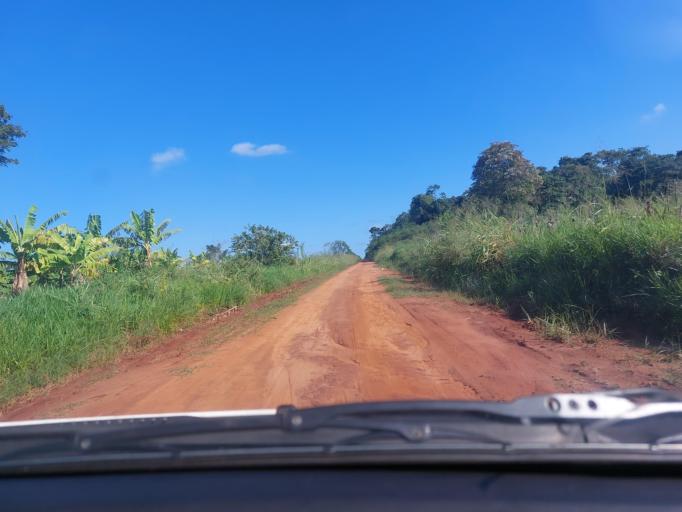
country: PY
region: San Pedro
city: Guayaybi
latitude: -24.5030
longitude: -56.5459
